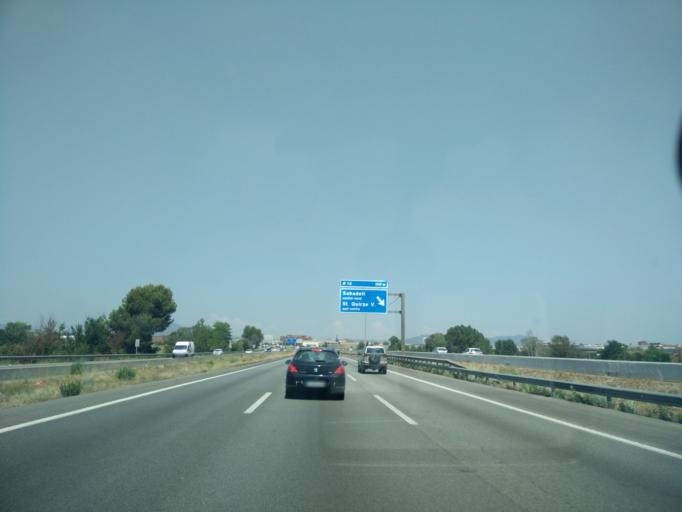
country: ES
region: Catalonia
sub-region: Provincia de Barcelona
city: Sant Quirze del Valles
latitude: 41.5201
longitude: 2.0976
